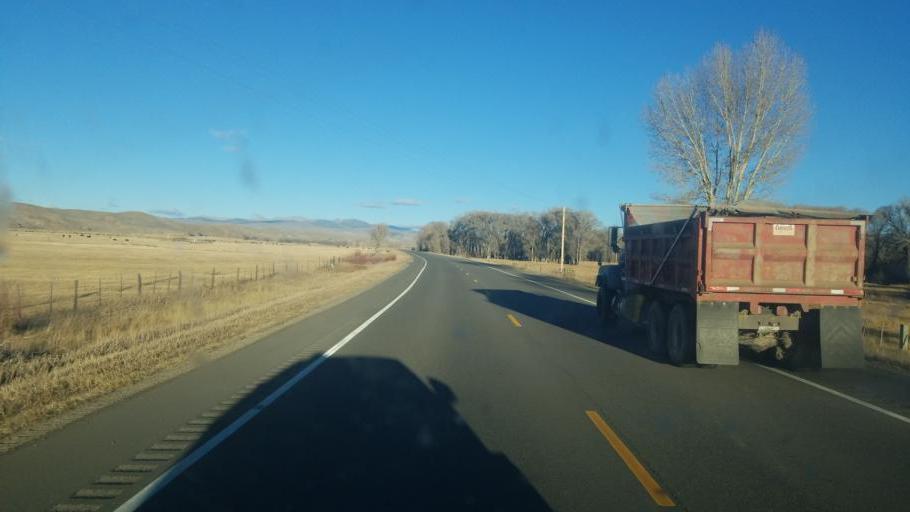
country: US
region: Colorado
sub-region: Gunnison County
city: Gunnison
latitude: 38.5172
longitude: -107.0134
